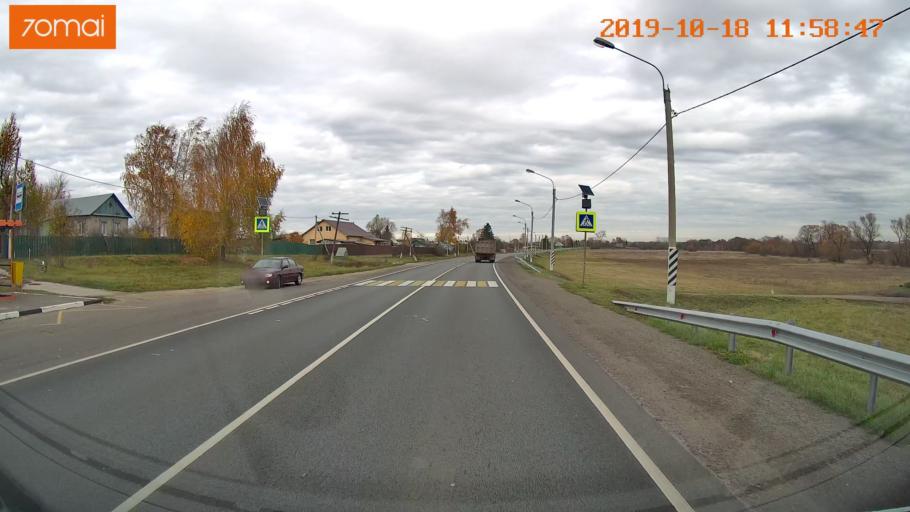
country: RU
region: Rjazan
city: Zakharovo
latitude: 54.2752
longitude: 39.1696
